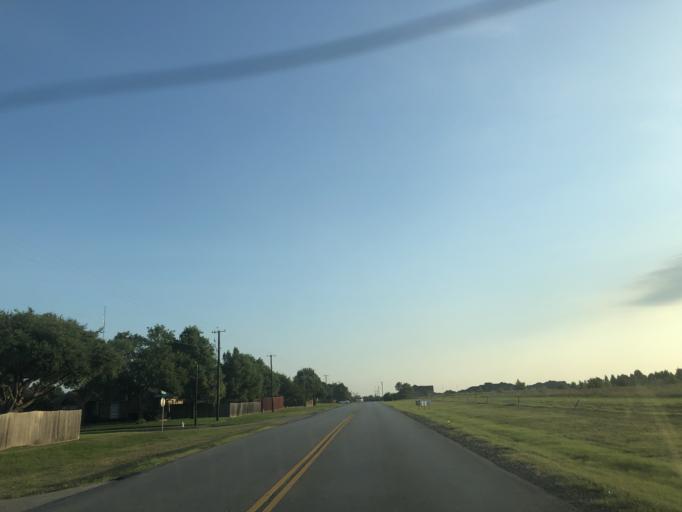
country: US
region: Texas
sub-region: Dallas County
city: Sunnyvale
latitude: 32.8377
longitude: -96.5606
